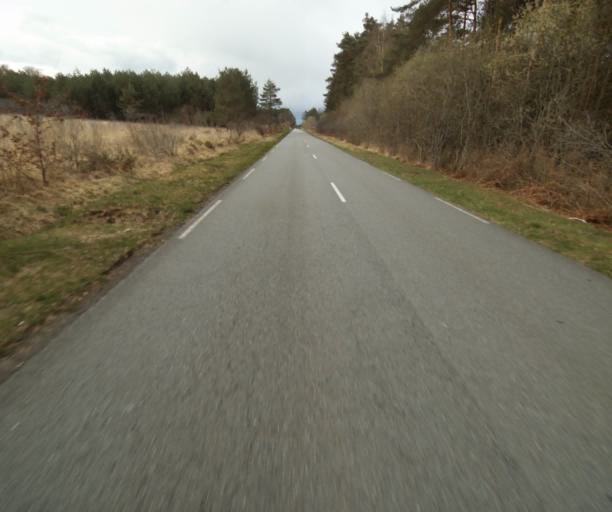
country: FR
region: Limousin
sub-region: Departement de la Correze
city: Saint-Privat
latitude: 45.2021
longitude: 2.0046
